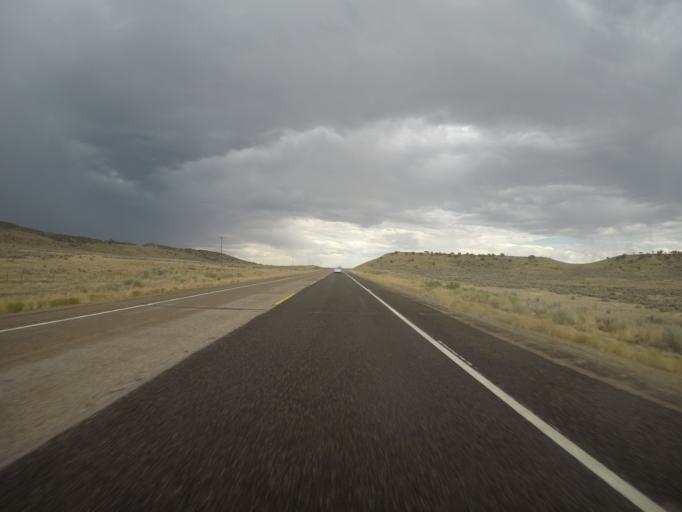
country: US
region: Colorado
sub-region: Rio Blanco County
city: Rangely
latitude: 40.2411
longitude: -108.9349
